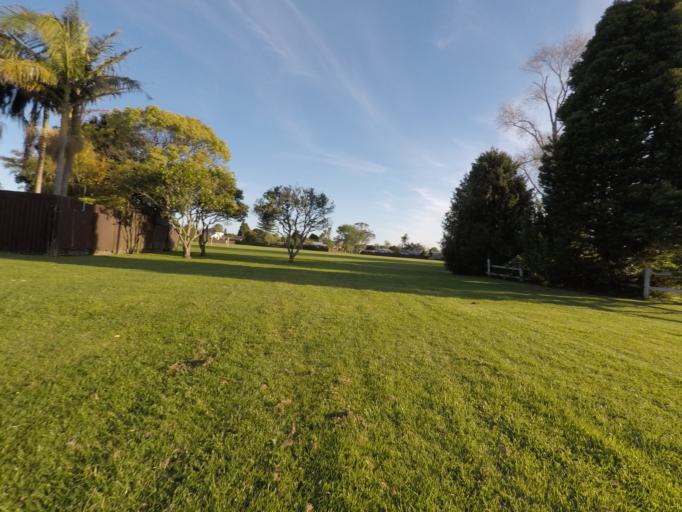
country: NZ
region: Auckland
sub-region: Auckland
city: Rosebank
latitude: -36.8422
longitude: 174.6487
